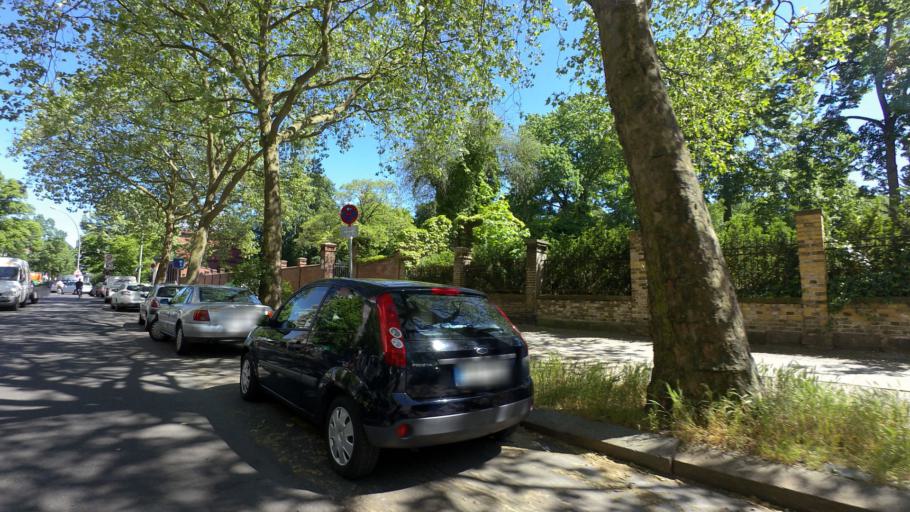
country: DE
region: Berlin
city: Bezirk Kreuzberg
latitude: 52.4888
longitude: 13.4044
